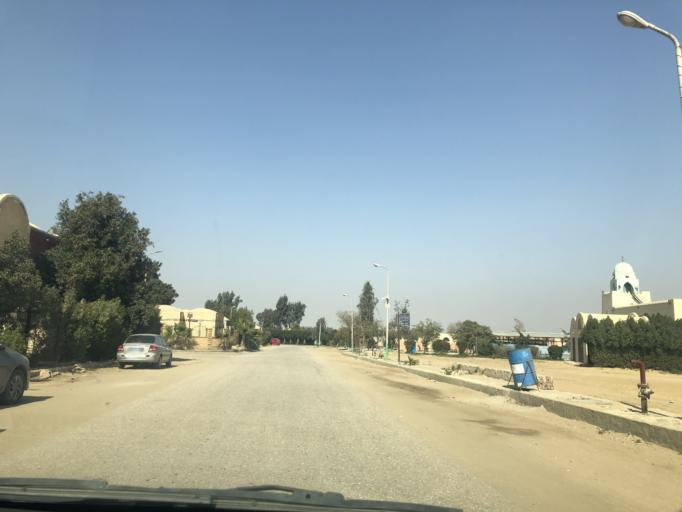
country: EG
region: Al Jizah
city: Madinat Sittah Uktubar
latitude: 29.9535
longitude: 31.0056
